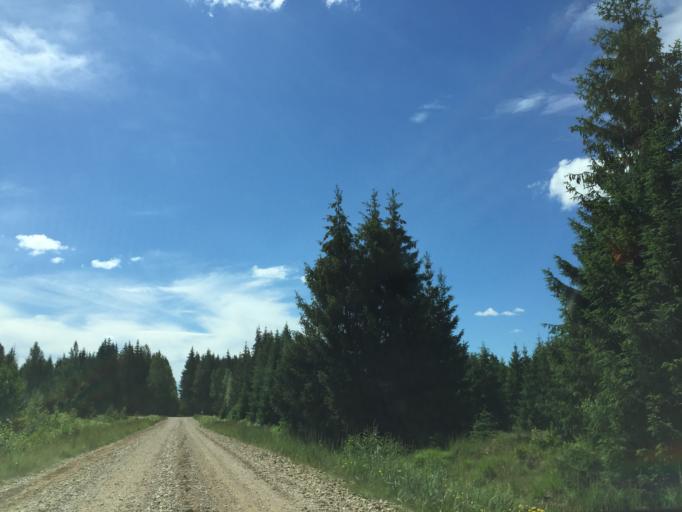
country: LV
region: Ventspils Rajons
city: Piltene
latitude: 57.2526
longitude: 21.8398
